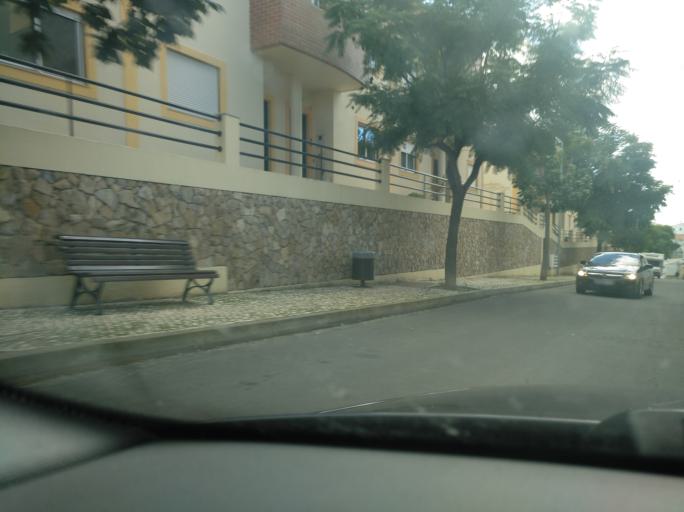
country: PT
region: Faro
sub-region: Tavira
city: Tavira
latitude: 37.1476
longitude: -7.6023
